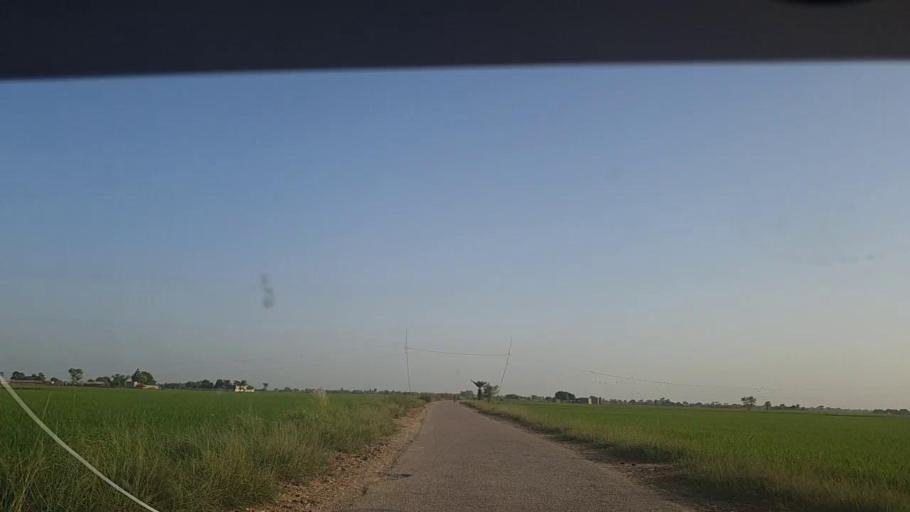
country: PK
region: Sindh
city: Thul
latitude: 28.1998
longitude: 68.8741
